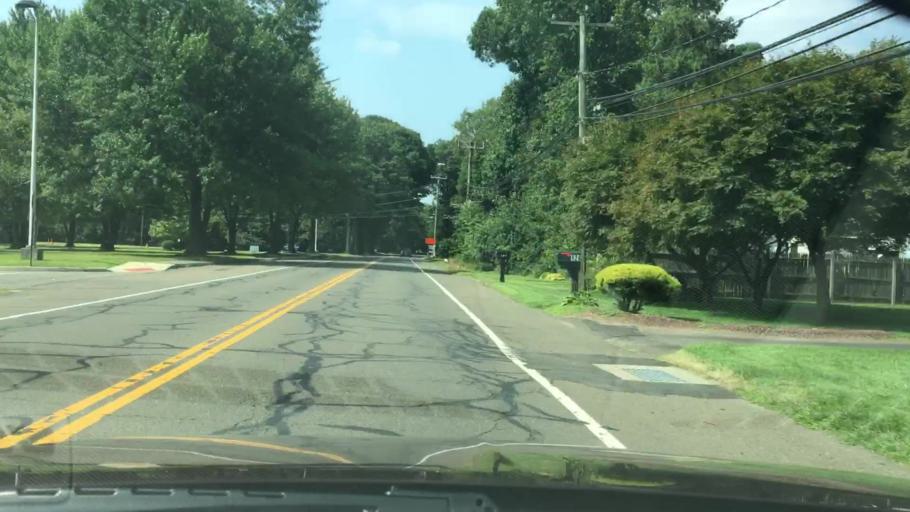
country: US
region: Connecticut
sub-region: Fairfield County
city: Norwalk
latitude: 41.1371
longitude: -73.4155
